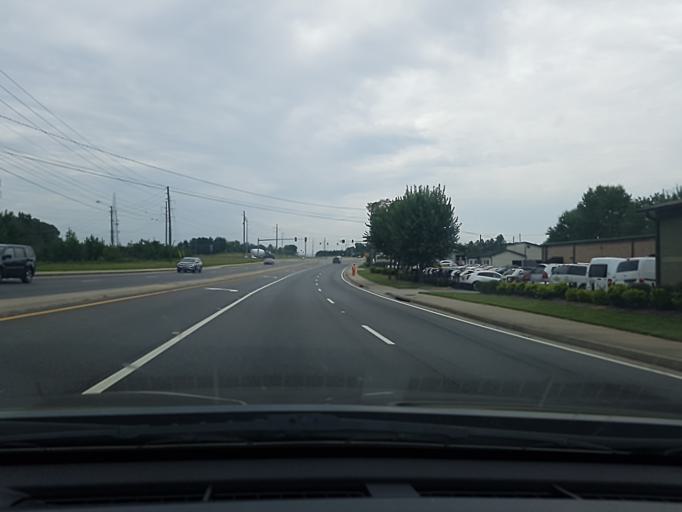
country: US
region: Georgia
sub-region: Gwinnett County
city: Duluth
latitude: 33.9839
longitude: -84.1547
